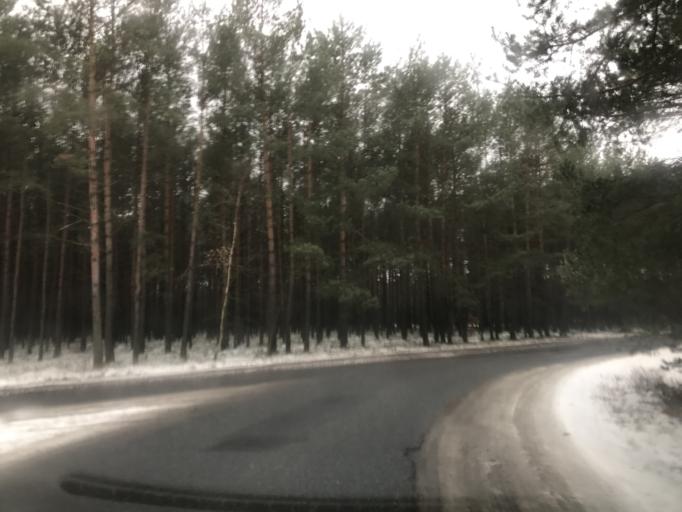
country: PL
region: Kujawsko-Pomorskie
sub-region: Powiat torunski
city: Wielka Nieszawka
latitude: 52.9839
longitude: 18.4859
